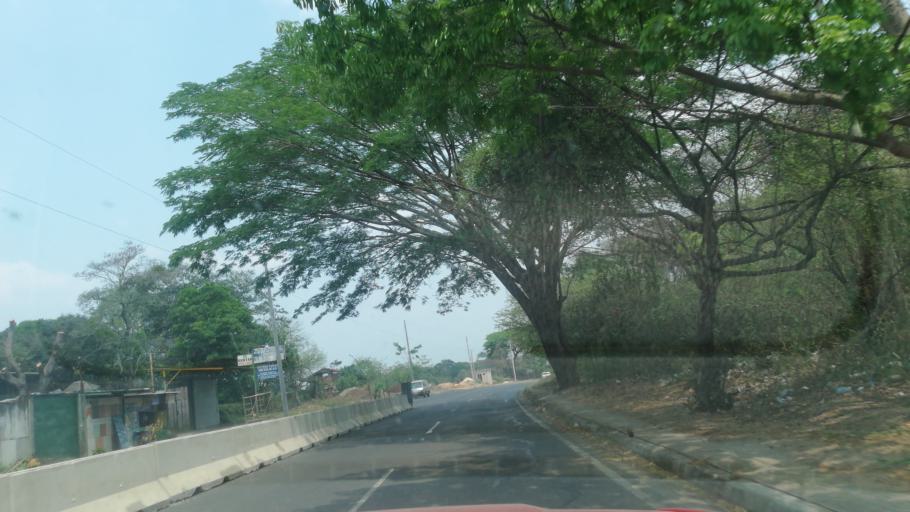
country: SV
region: Santa Ana
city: Santa Ana
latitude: 13.9775
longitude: -89.5931
